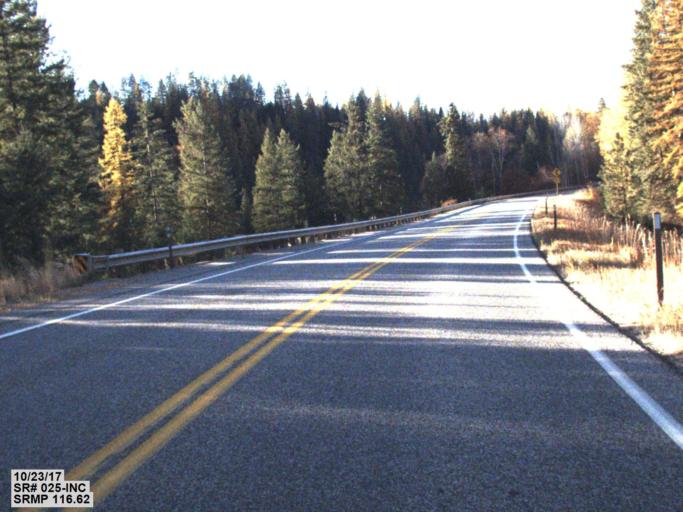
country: CA
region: British Columbia
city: Rossland
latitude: 48.9444
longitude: -117.7902
